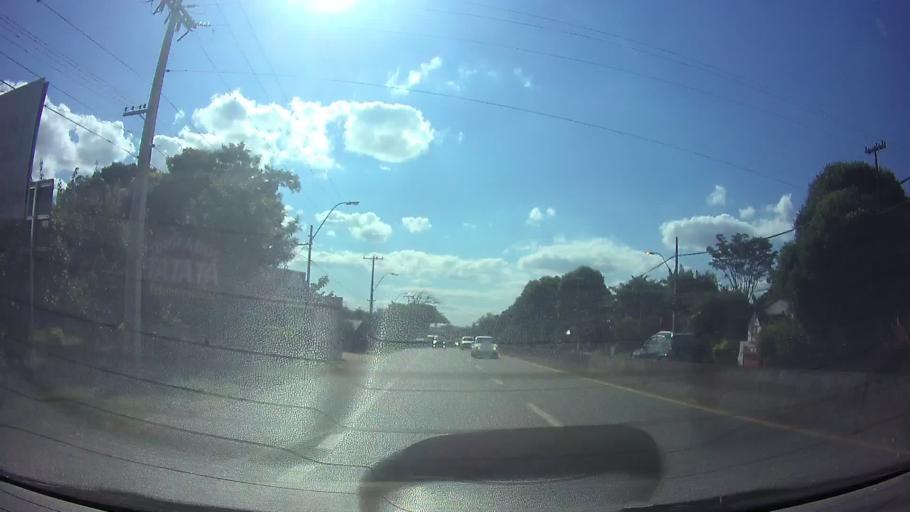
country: PY
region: Central
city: Itaugua
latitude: -25.3969
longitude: -57.3421
